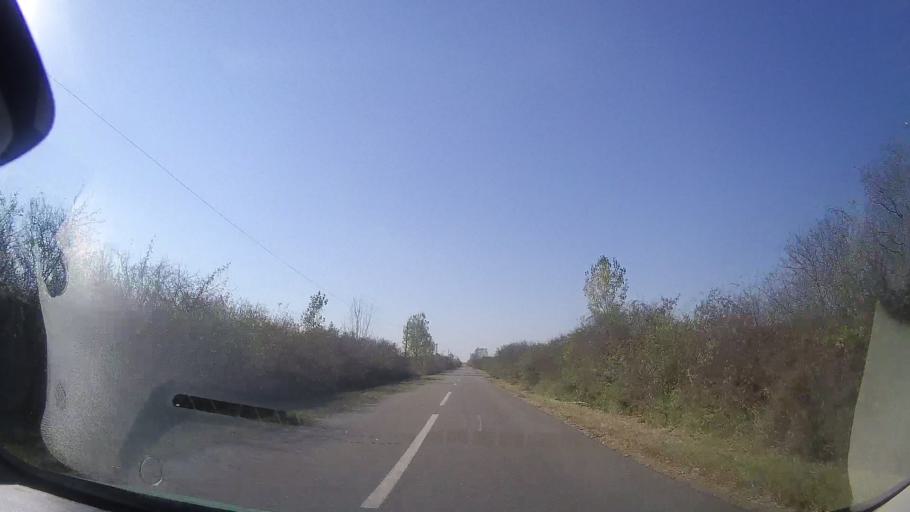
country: RO
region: Timis
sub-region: Comuna Secas
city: Secas
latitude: 45.8739
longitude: 21.8157
